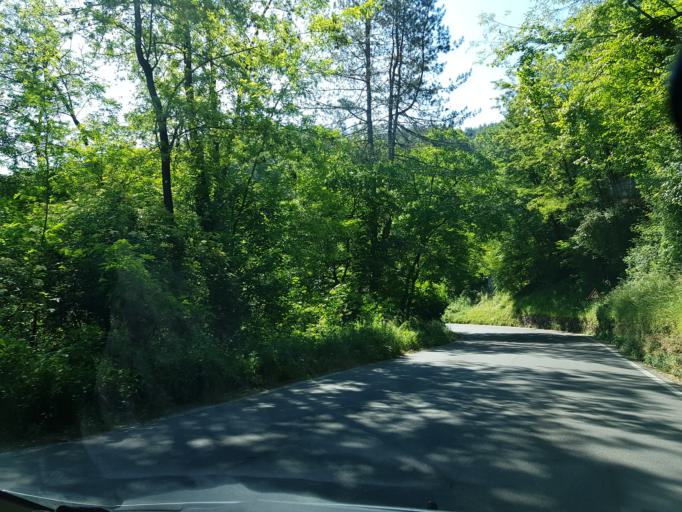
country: IT
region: Tuscany
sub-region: Provincia di Lucca
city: Camporgiano
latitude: 44.1692
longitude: 10.3192
